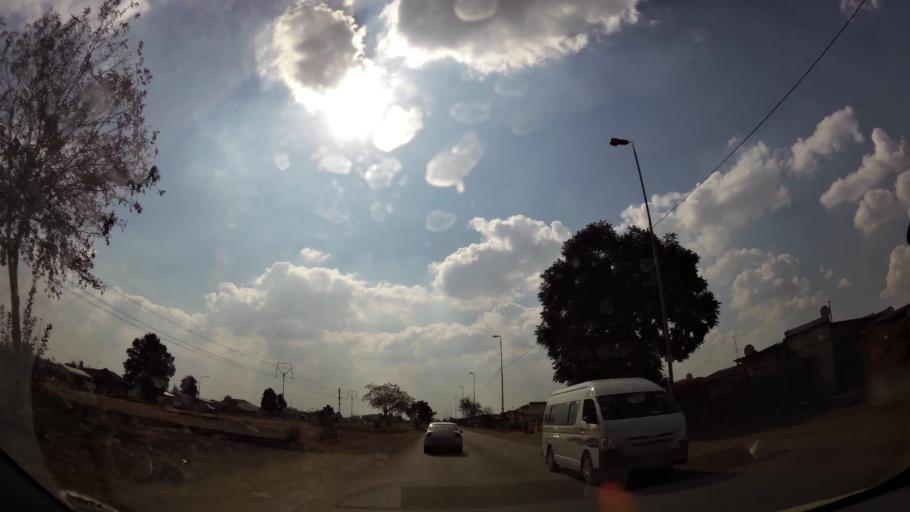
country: ZA
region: Gauteng
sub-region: Ekurhuleni Metropolitan Municipality
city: Germiston
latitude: -26.3394
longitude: 28.1439
